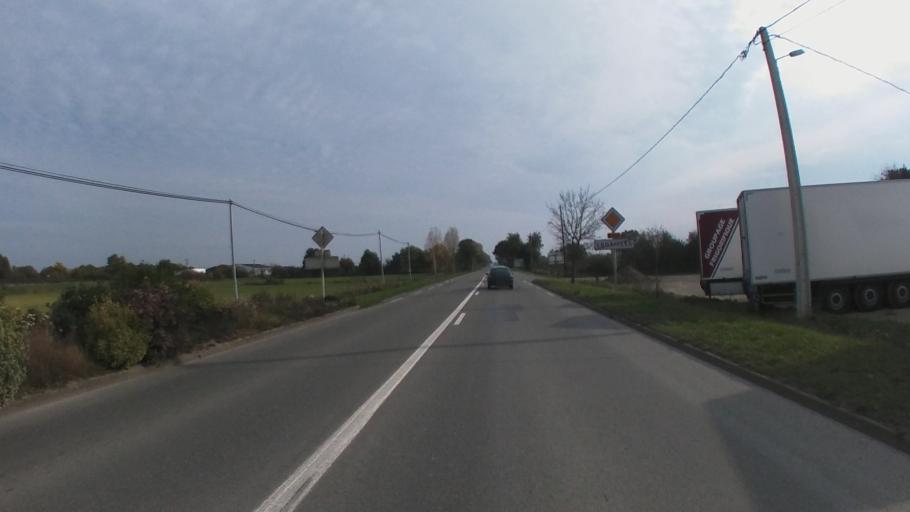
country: FR
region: Pays de la Loire
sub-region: Departement de la Sarthe
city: Vion
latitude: 47.7913
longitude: -0.2496
